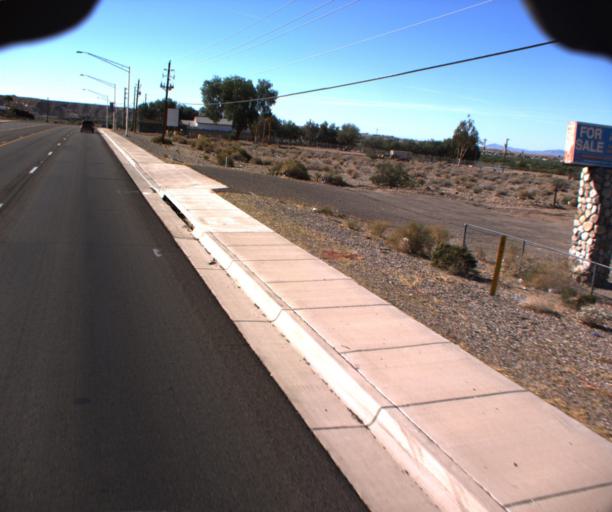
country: US
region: Arizona
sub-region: Mohave County
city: Bullhead City
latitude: 35.0721
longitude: -114.5907
